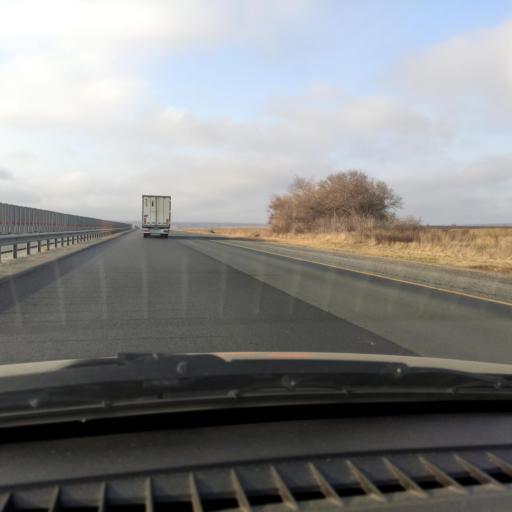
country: RU
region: Samara
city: Kurumoch
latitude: 53.5050
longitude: 49.9826
